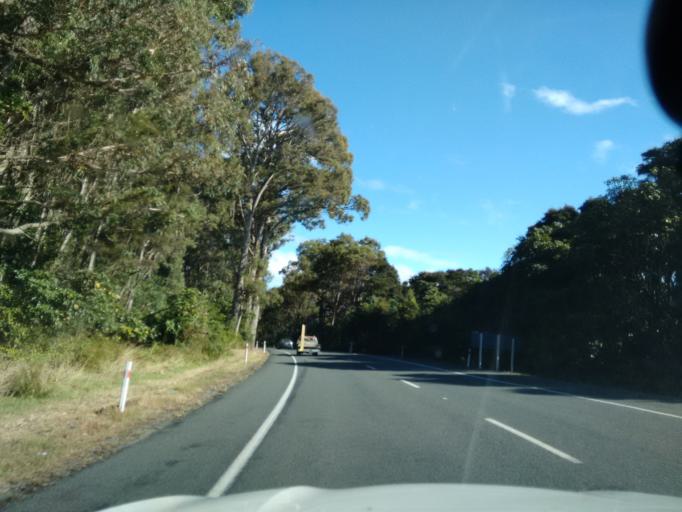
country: NZ
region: Waikato
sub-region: Taupo District
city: Taupo
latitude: -38.8574
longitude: 176.0117
